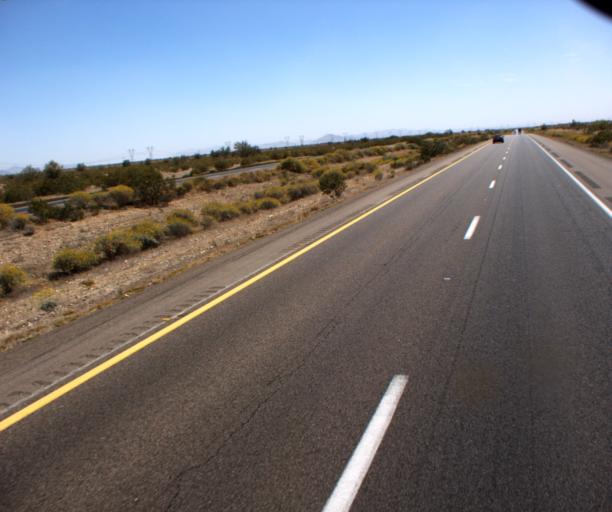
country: US
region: Arizona
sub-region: Maricopa County
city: Gila Bend
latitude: 33.0705
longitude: -112.6462
